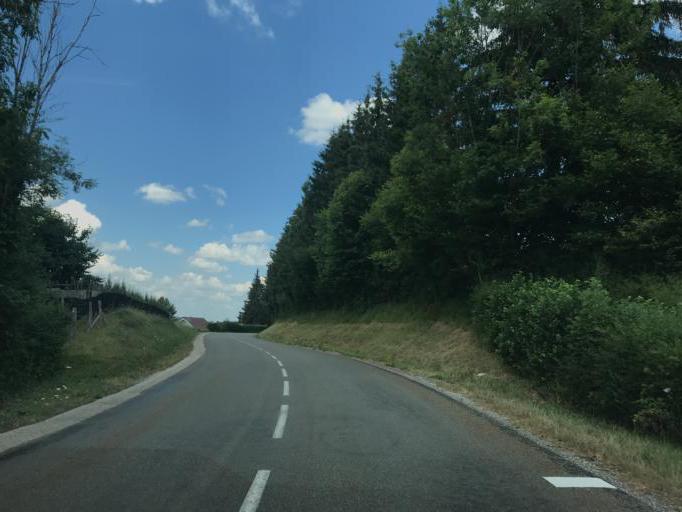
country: FR
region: Franche-Comte
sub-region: Departement du Jura
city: Clairvaux-les-Lacs
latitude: 46.5677
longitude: 5.7567
